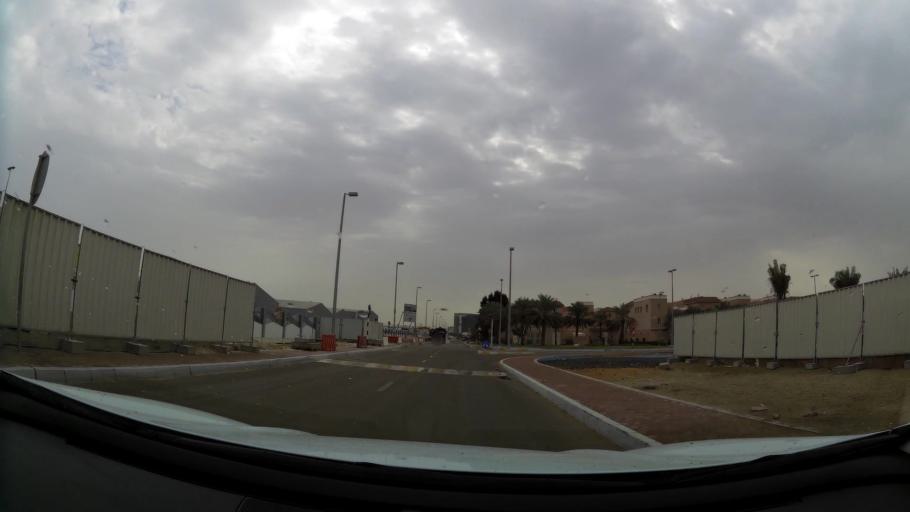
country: AE
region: Abu Dhabi
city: Abu Dhabi
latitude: 24.4300
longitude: 54.4478
